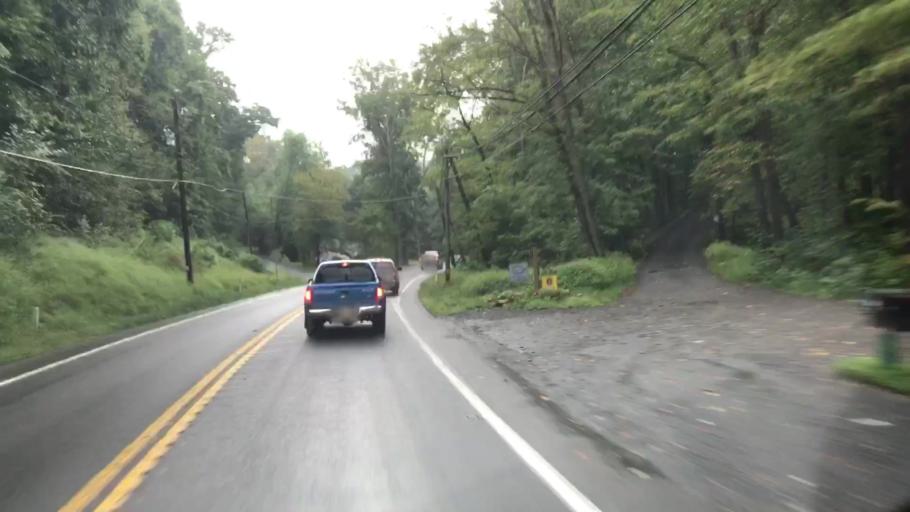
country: US
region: Pennsylvania
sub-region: Cumberland County
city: Schlusser
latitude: 40.3039
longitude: -77.1522
